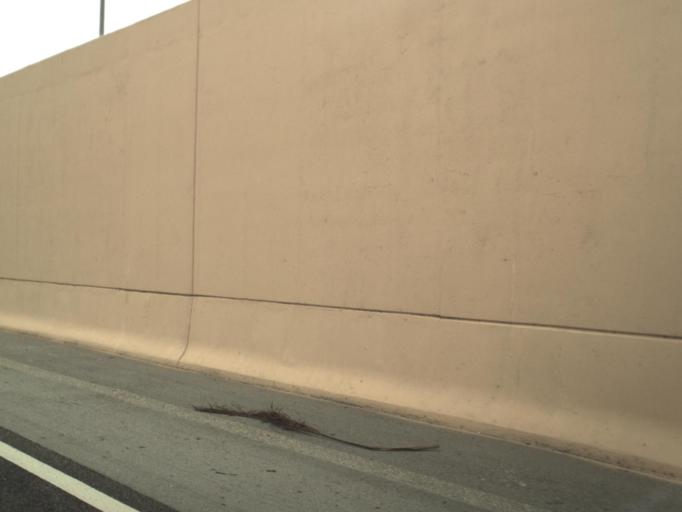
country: US
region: Florida
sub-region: Miami-Dade County
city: Sunset
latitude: 25.6945
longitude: -80.3454
